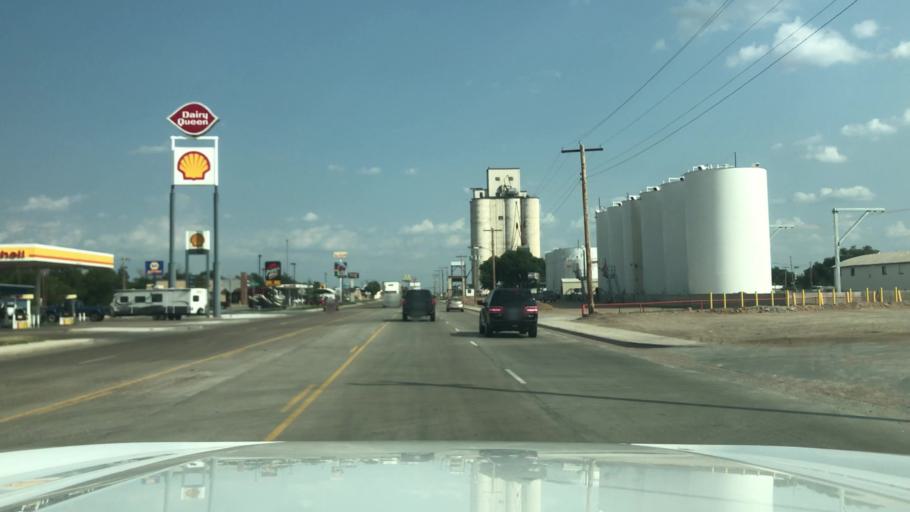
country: US
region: Texas
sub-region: Dallam County
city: Dalhart
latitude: 36.0638
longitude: -102.5193
